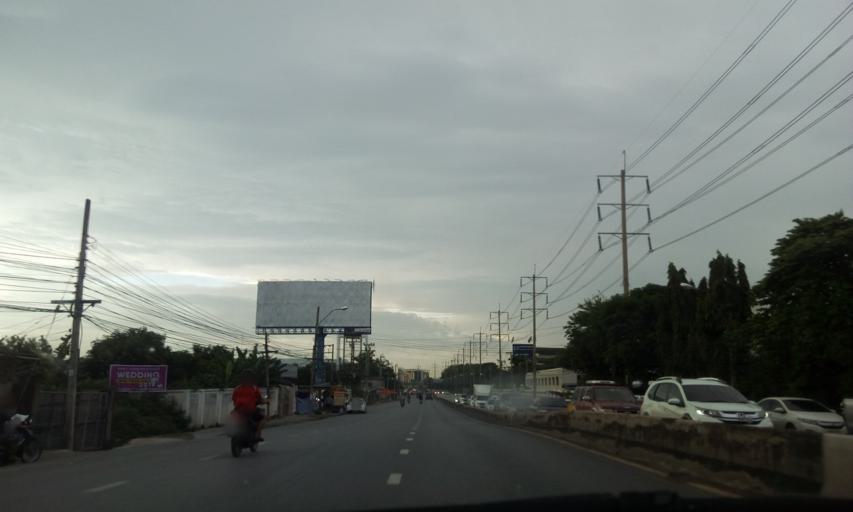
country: TH
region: Phra Nakhon Si Ayutthaya
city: Ban Bang Kadi Pathum Thani
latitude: 13.9527
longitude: 100.5484
